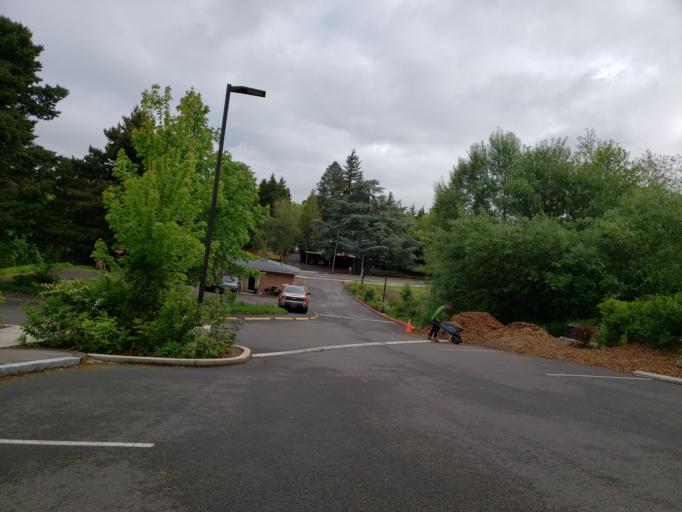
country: US
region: Oregon
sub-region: Washington County
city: Garden Home-Whitford
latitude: 45.4754
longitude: -122.7245
